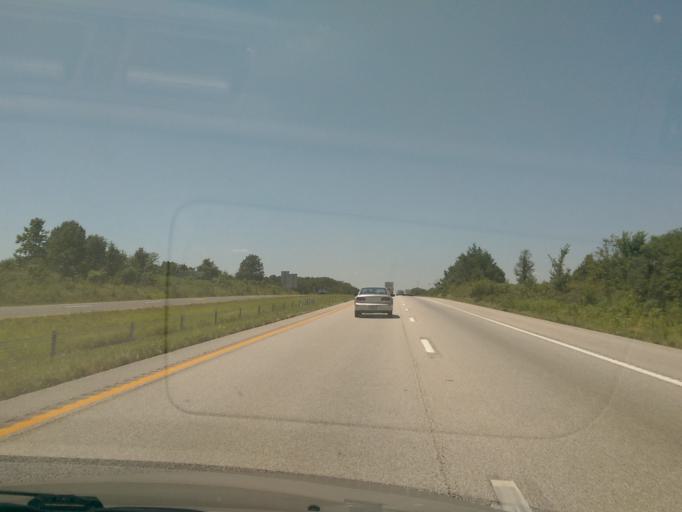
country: US
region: Missouri
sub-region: Saline County
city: Marshall
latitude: 38.9479
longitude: -93.0095
